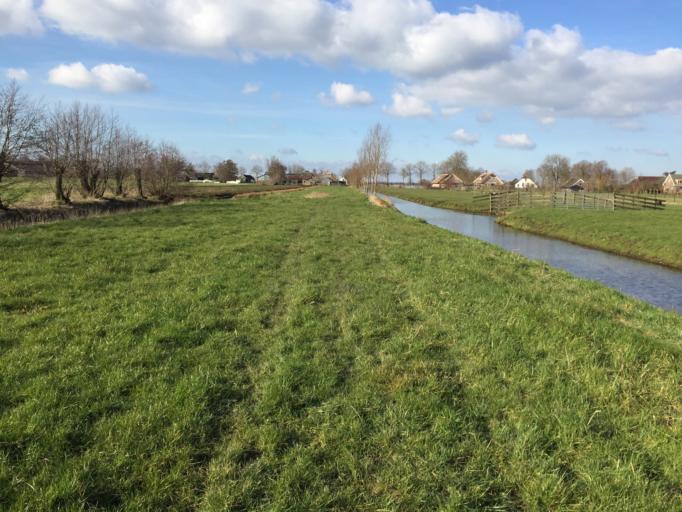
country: NL
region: Utrecht
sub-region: Gemeente Lopik
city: Lopik
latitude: 51.9966
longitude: 4.9239
